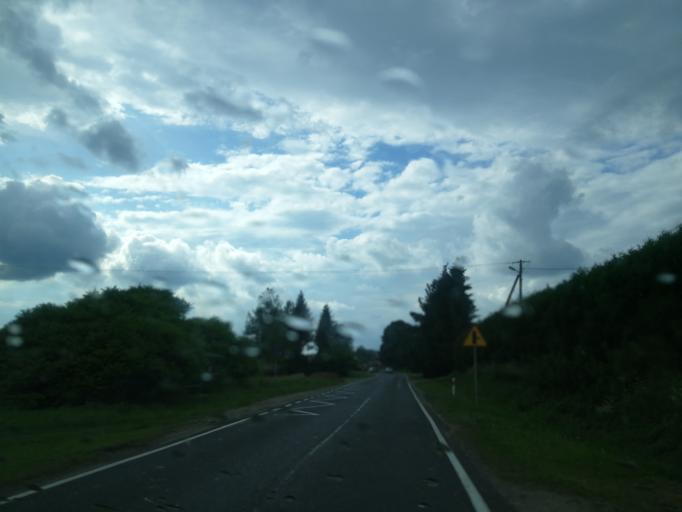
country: PL
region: Subcarpathian Voivodeship
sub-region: Powiat leski
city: Uherce Mineralne
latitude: 49.4567
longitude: 22.4162
